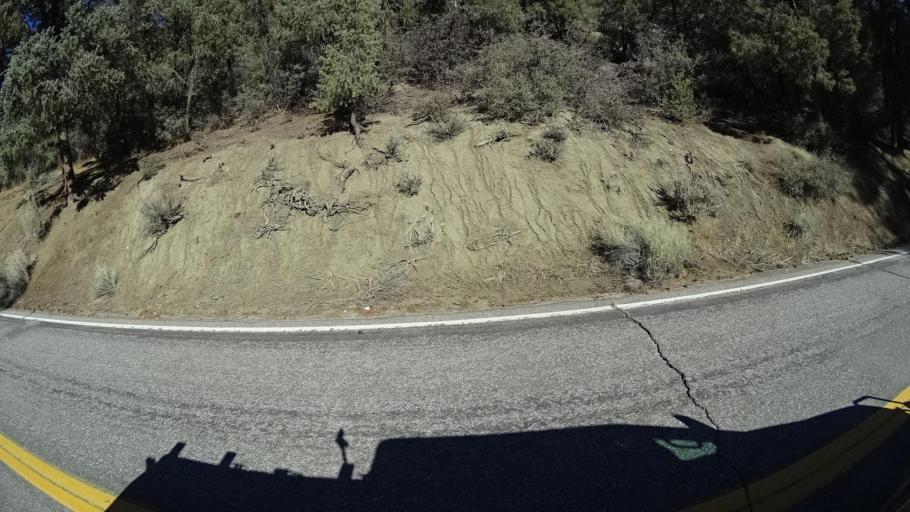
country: US
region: California
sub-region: Kern County
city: Pine Mountain Club
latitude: 34.8606
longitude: -119.2033
